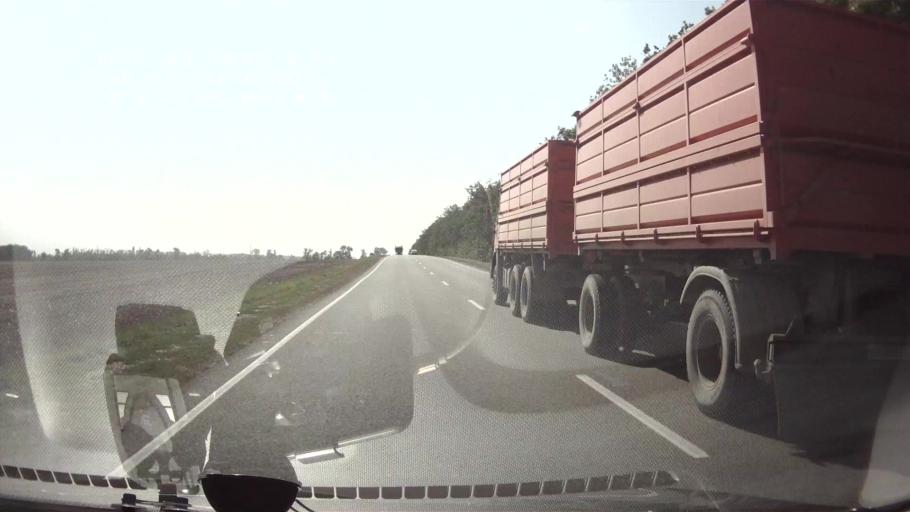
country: RU
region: Krasnodarskiy
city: Kavkazskaya
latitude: 45.5050
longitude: 40.6804
